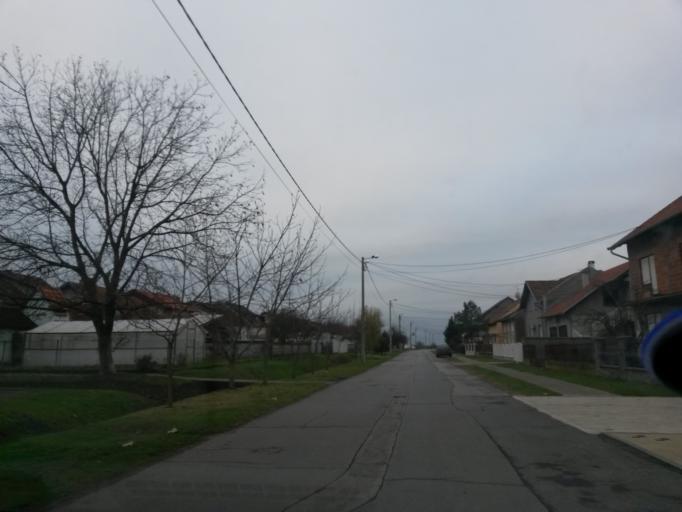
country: HR
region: Osjecko-Baranjska
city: Tenja
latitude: 45.5120
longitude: 18.7340
